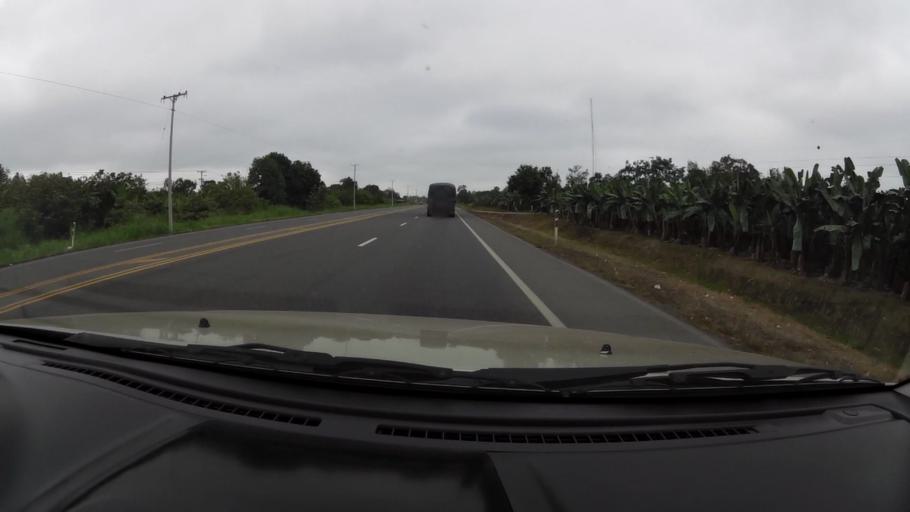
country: EC
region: Guayas
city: Naranjal
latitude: -2.5666
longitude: -79.5694
